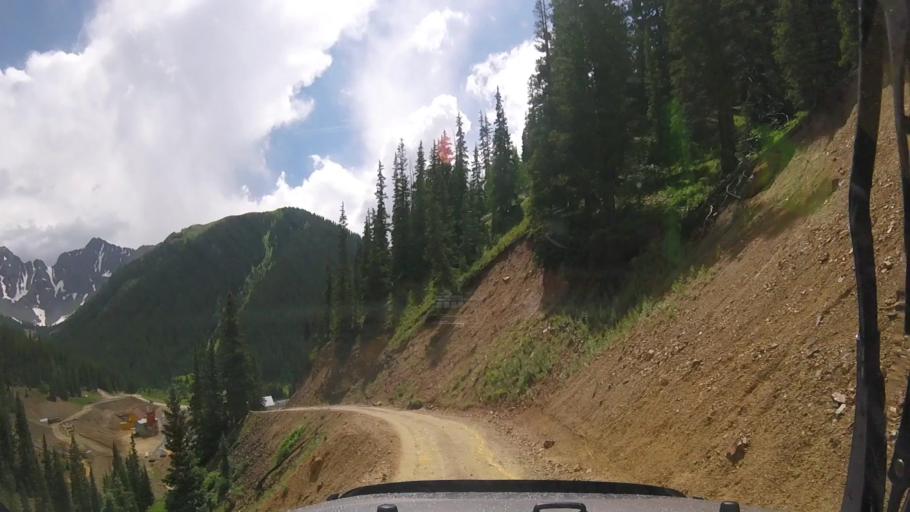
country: US
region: Colorado
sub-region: San Juan County
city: Silverton
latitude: 37.8930
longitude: -107.6488
